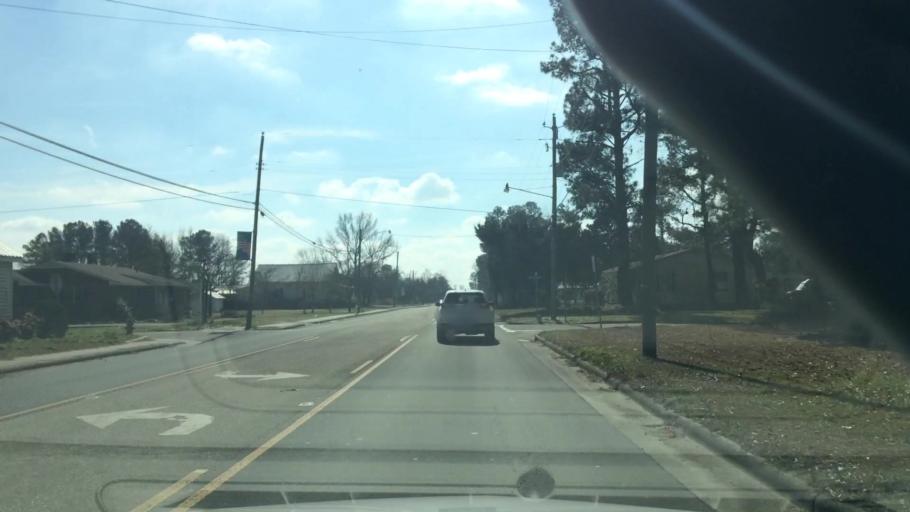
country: US
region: North Carolina
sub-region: Duplin County
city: Beulaville
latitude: 34.9222
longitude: -77.7741
